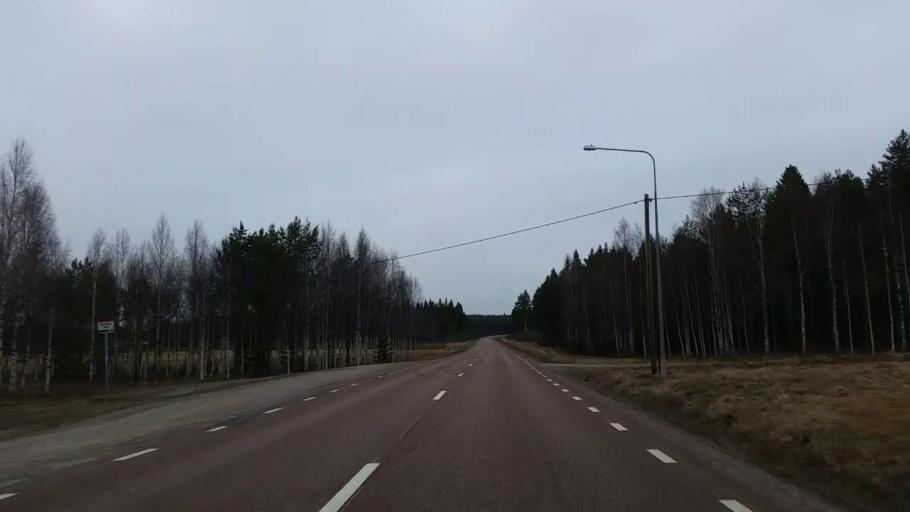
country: SE
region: Gaevleborg
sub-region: Ovanakers Kommun
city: Edsbyn
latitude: 61.2725
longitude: 15.8938
